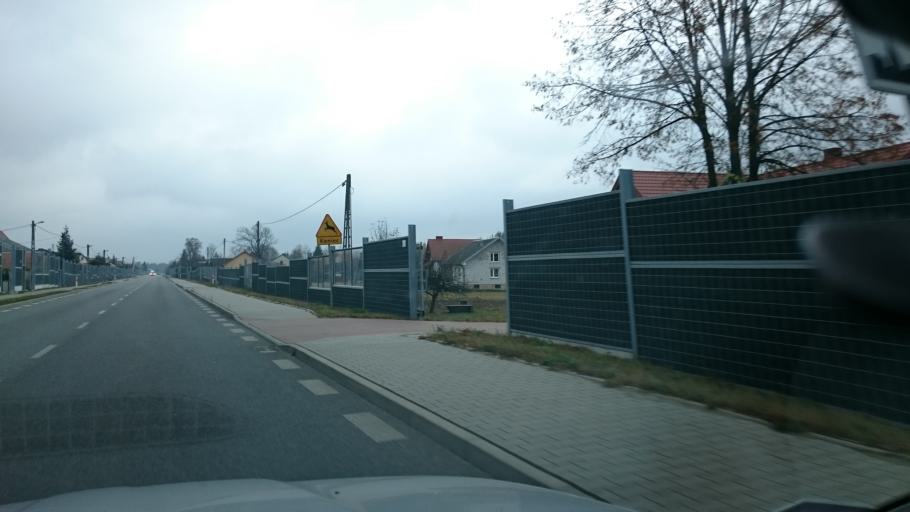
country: PL
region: Swietokrzyskie
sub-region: Powiat konecki
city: Konskie
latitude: 51.1484
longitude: 20.3619
